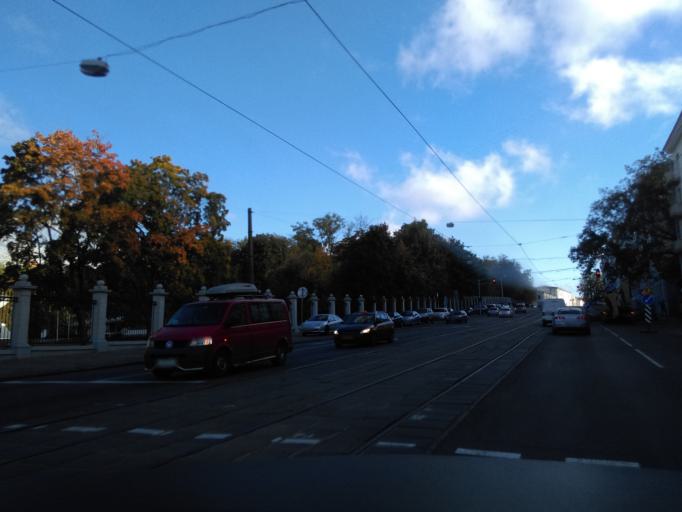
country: BY
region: Minsk
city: Minsk
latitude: 53.9003
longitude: 27.5742
